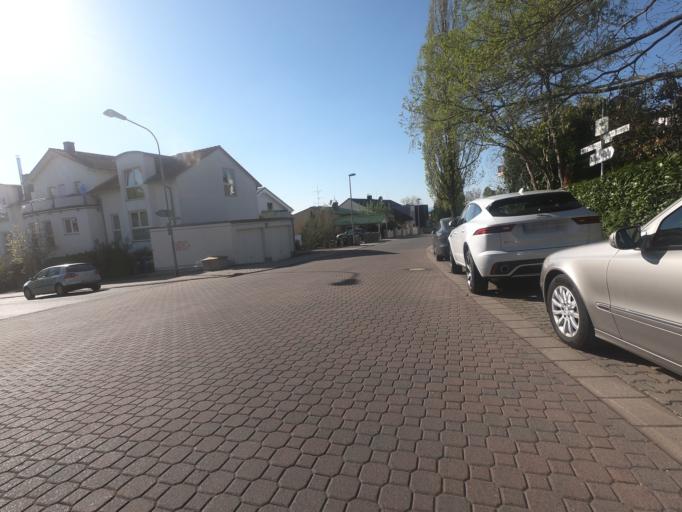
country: DE
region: Hesse
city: Langen
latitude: 49.9836
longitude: 8.6884
